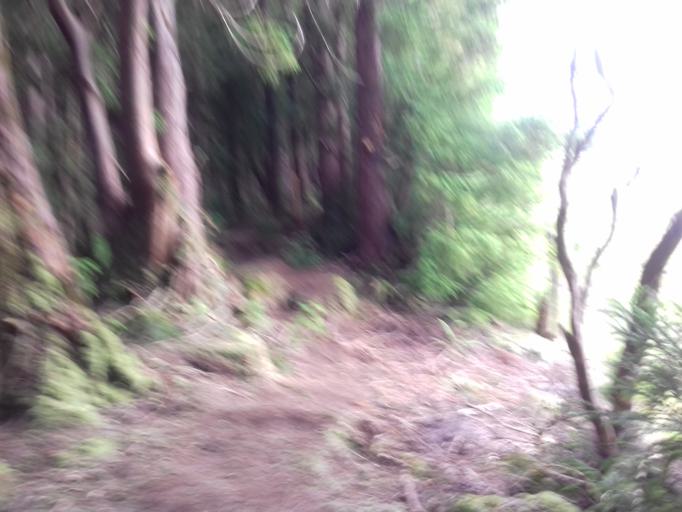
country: PT
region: Azores
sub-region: Praia da Vitoria
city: Biscoitos
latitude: 38.7303
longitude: -27.2820
